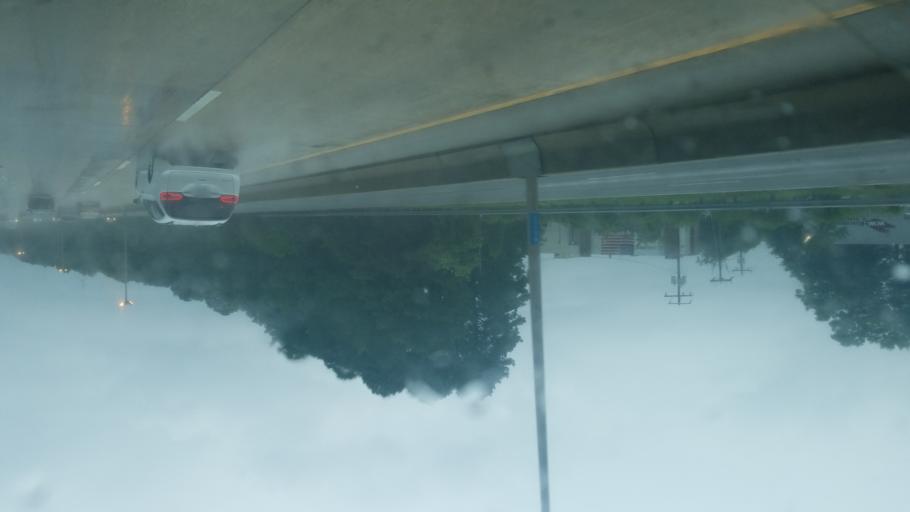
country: US
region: Virginia
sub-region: City of Newport News
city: Newport News
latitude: 37.0114
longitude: -76.3956
